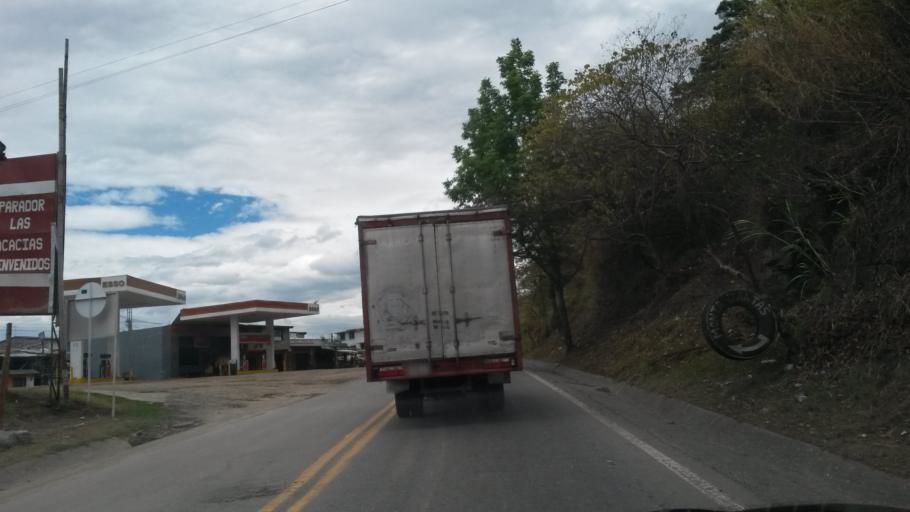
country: CO
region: Cauca
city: Rosas
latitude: 2.2652
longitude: -76.7392
